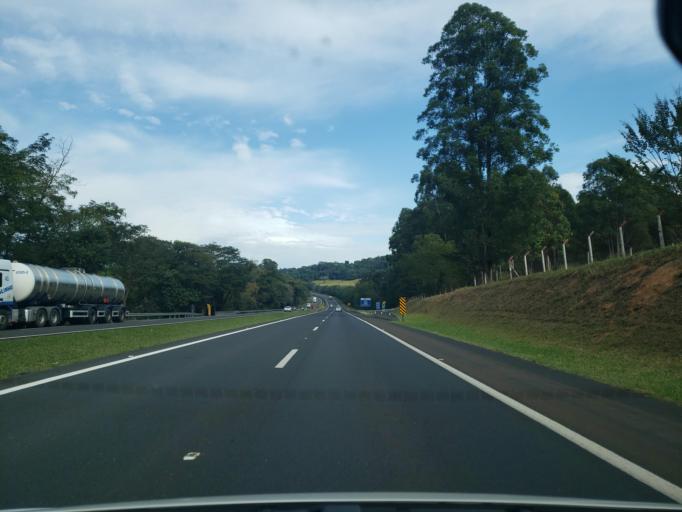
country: BR
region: Sao Paulo
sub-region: Brotas
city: Brotas
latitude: -22.2766
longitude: -47.9792
